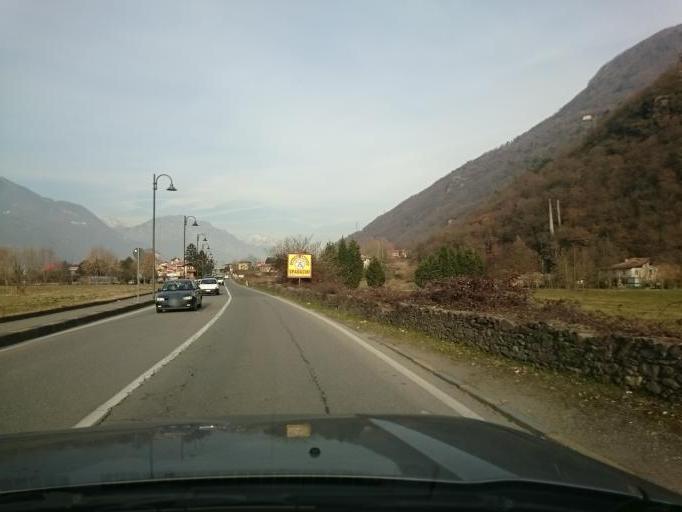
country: IT
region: Lombardy
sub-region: Provincia di Brescia
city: Pisogne
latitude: 45.8124
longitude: 10.1140
